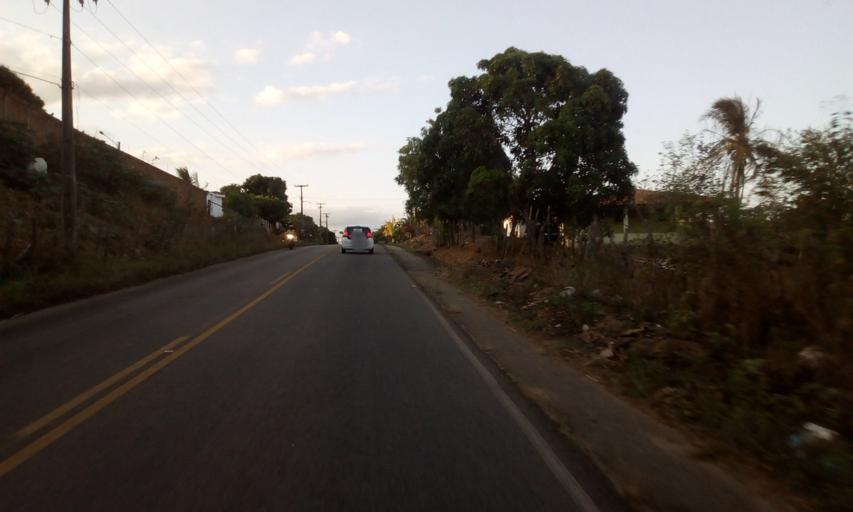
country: BR
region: Paraiba
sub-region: Guarabira
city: Guarabira
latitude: -6.9070
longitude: -35.4556
